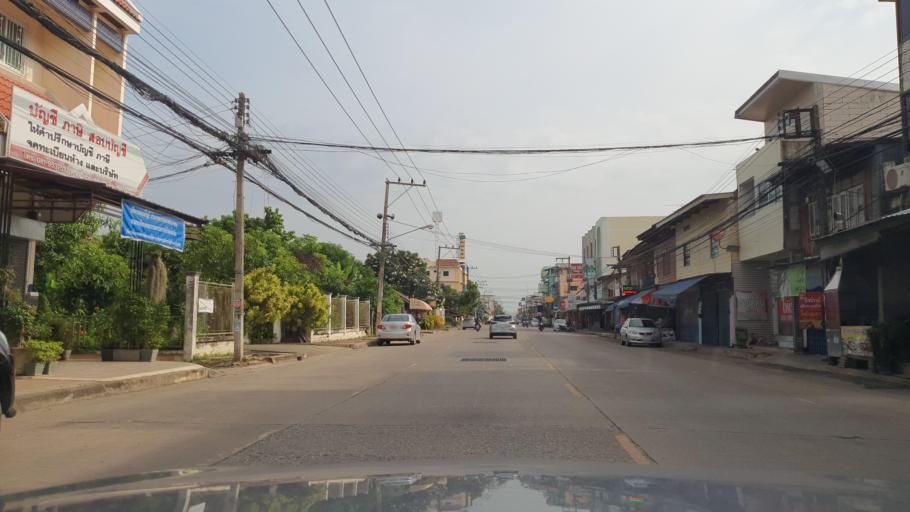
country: TH
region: Phitsanulok
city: Phitsanulok
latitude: 16.8311
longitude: 100.2655
